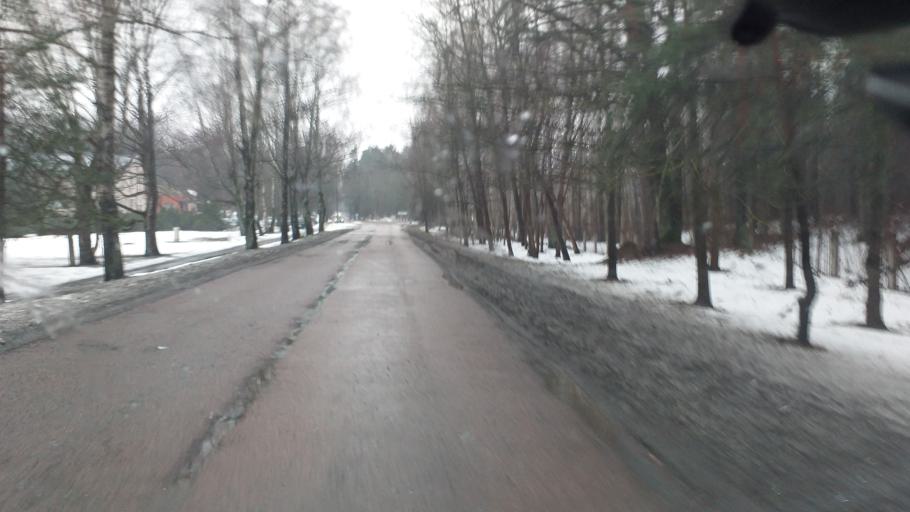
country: LV
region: Riga
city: Bolderaja
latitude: 56.9846
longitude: 24.0277
